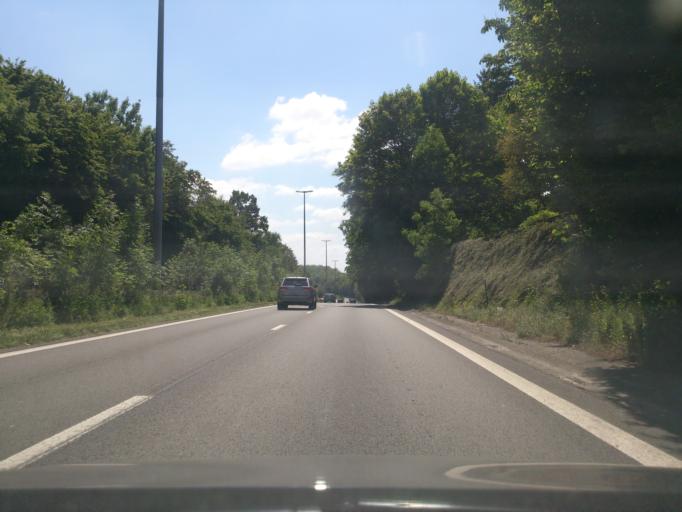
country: BE
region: Wallonia
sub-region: Province du Brabant Wallon
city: Waterloo
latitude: 50.7246
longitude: 4.4162
